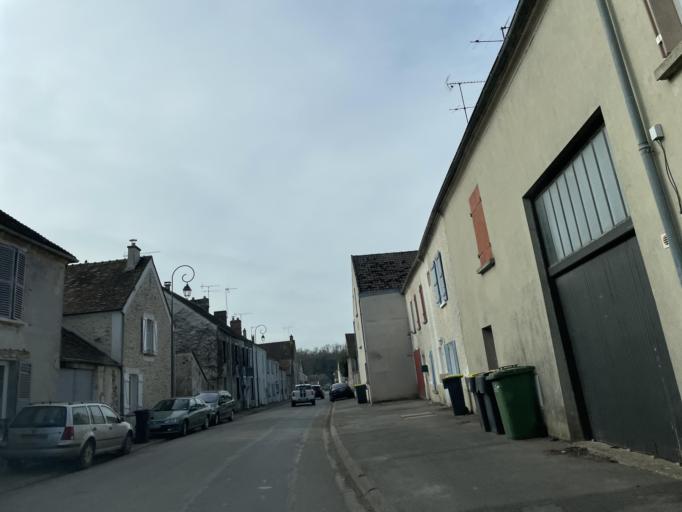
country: FR
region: Ile-de-France
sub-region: Departement de Seine-et-Marne
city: Chailly-en-Brie
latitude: 48.7429
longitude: 3.1296
